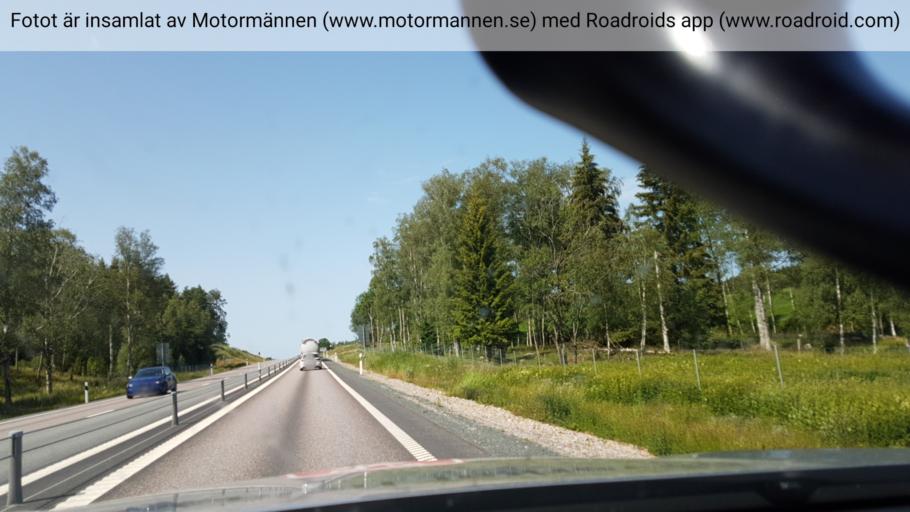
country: SE
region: Joenkoeping
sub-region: Aneby Kommun
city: Aneby
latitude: 57.8077
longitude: 14.8650
